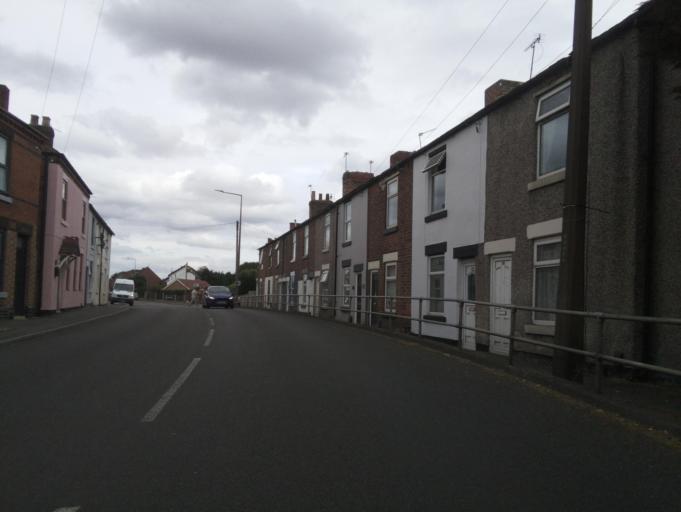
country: GB
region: England
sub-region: Derbyshire
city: Borrowash
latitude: 52.9046
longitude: -1.3737
